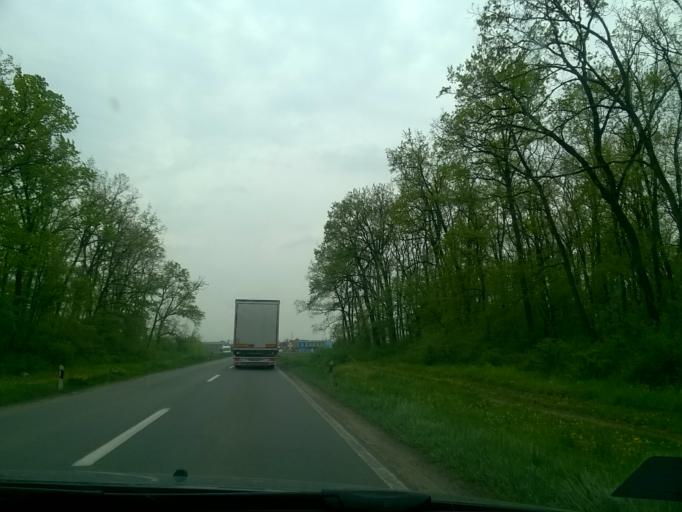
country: RS
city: Hrtkovci
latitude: 44.8945
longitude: 19.7640
